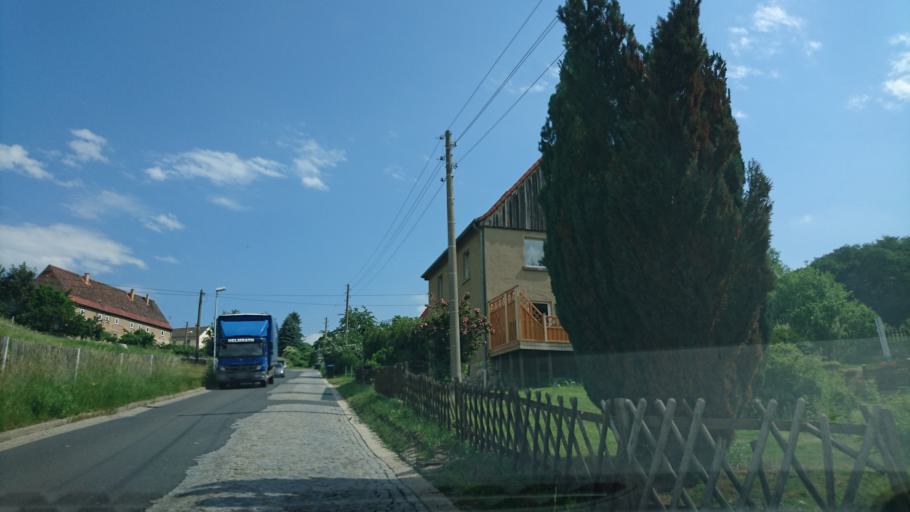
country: DE
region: Saxony
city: Struppen
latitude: 50.9255
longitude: 13.9803
